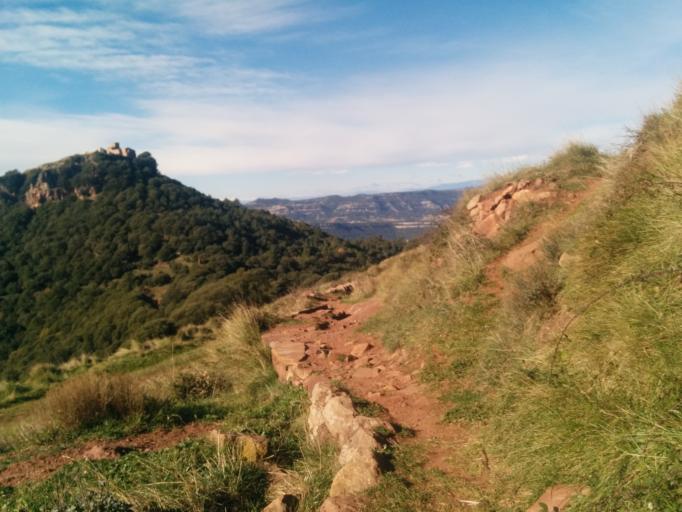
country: ES
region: Catalonia
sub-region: Provincia de Barcelona
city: Tagamanent
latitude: 41.7475
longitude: 2.3024
